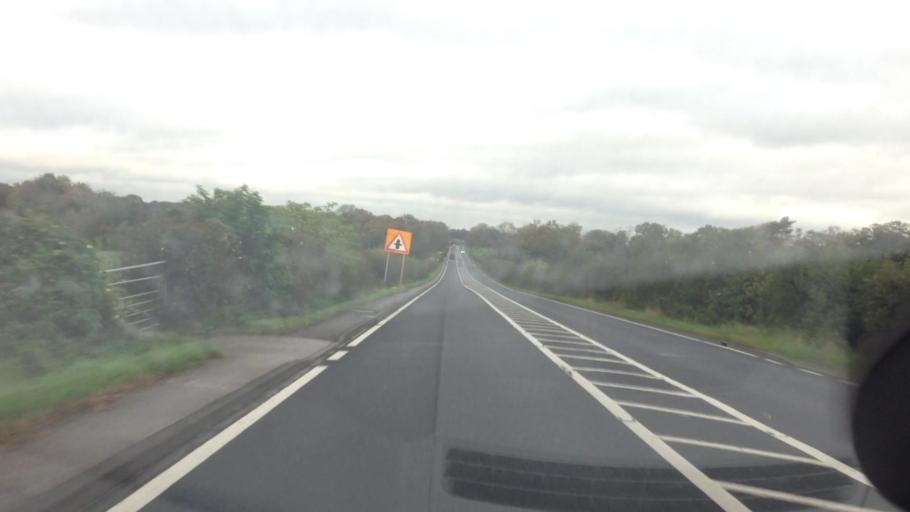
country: GB
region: England
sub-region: City and Borough of Leeds
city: Shadwell
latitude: 53.8467
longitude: -1.4658
